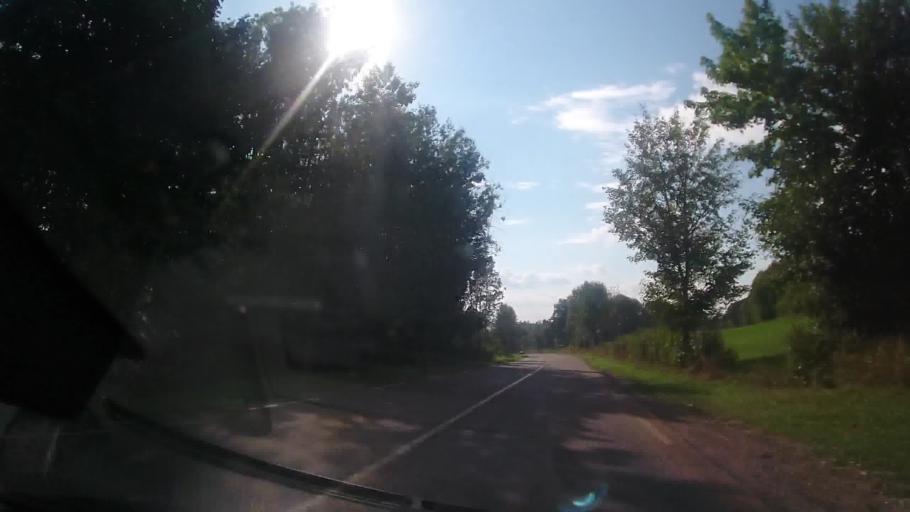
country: FR
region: Franche-Comte
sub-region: Departement du Jura
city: Clairvaux-les-Lacs
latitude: 46.5831
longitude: 5.8038
